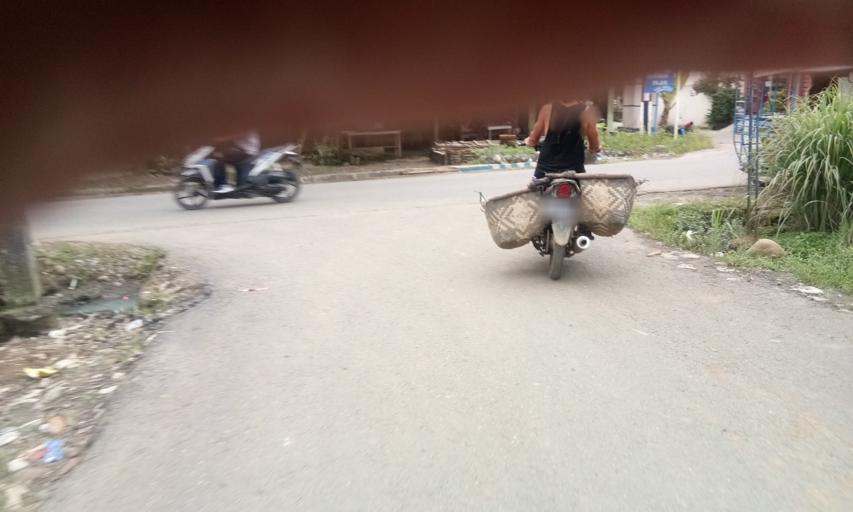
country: ID
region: North Sumatra
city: Deli Tua
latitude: 3.4780
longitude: 98.6097
